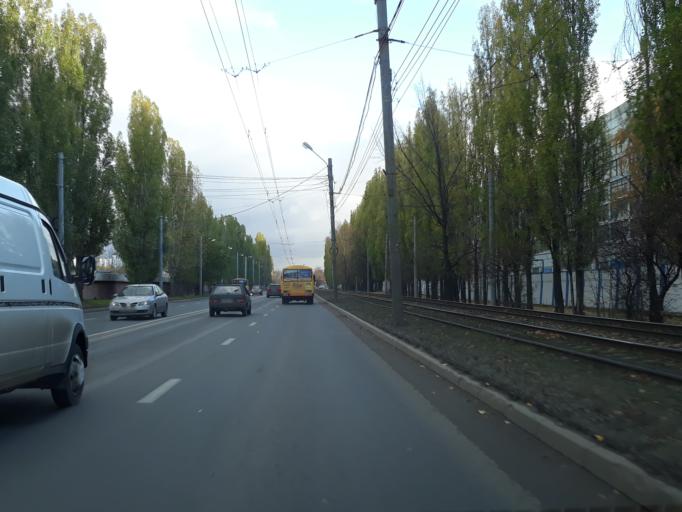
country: RU
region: Nizjnij Novgorod
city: Nizhniy Novgorod
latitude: 56.3329
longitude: 43.8951
